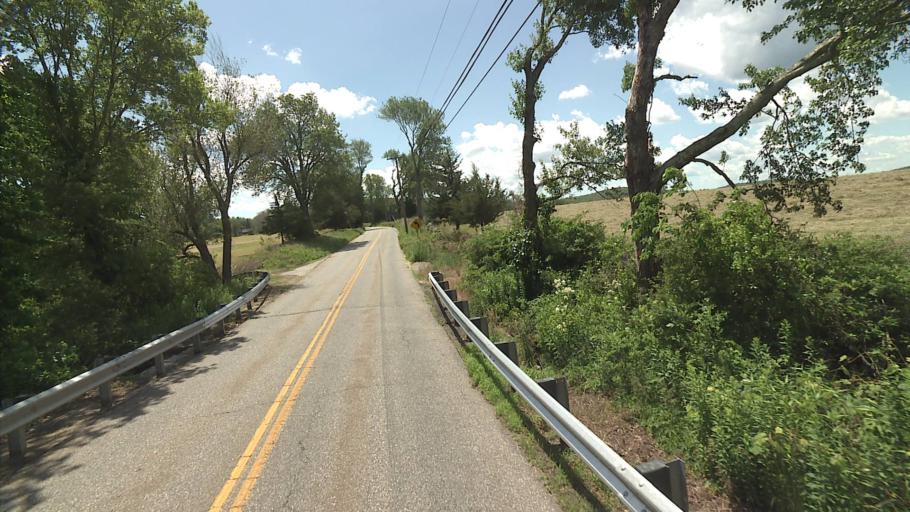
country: US
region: Connecticut
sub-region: New London County
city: Preston City
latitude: 41.5386
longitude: -71.8805
